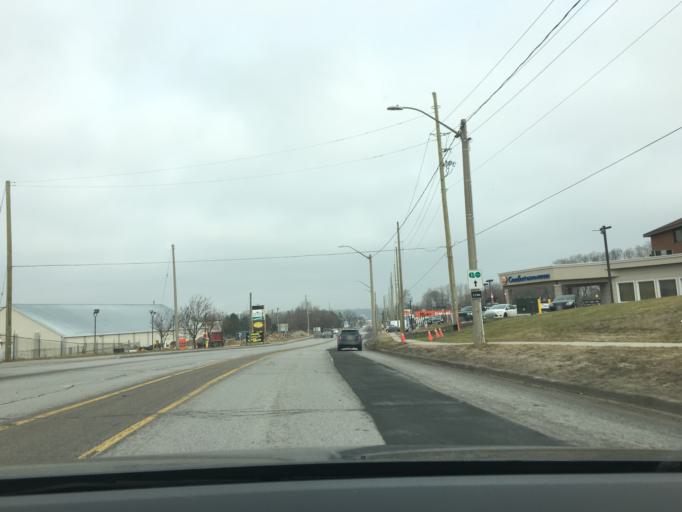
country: CA
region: Ontario
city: Barrie
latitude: 44.3648
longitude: -79.6971
